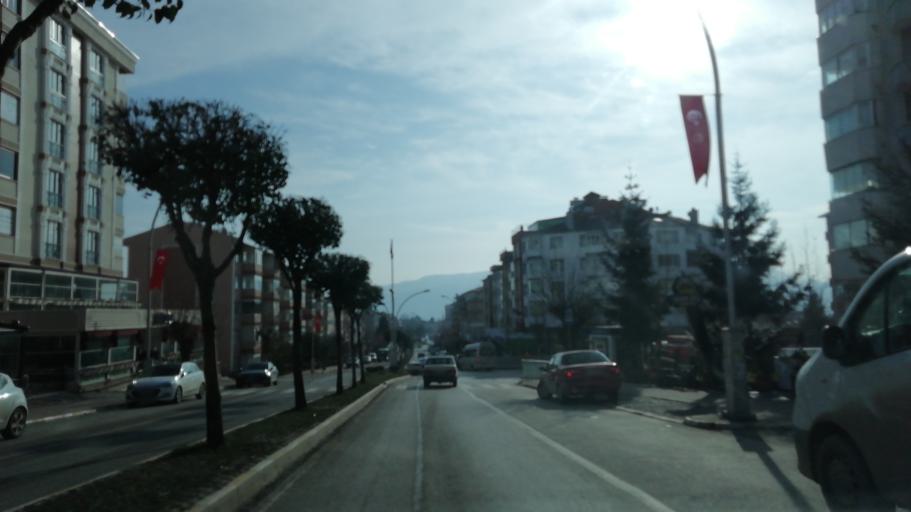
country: TR
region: Karabuk
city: Safranbolu
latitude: 41.2532
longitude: 32.6787
